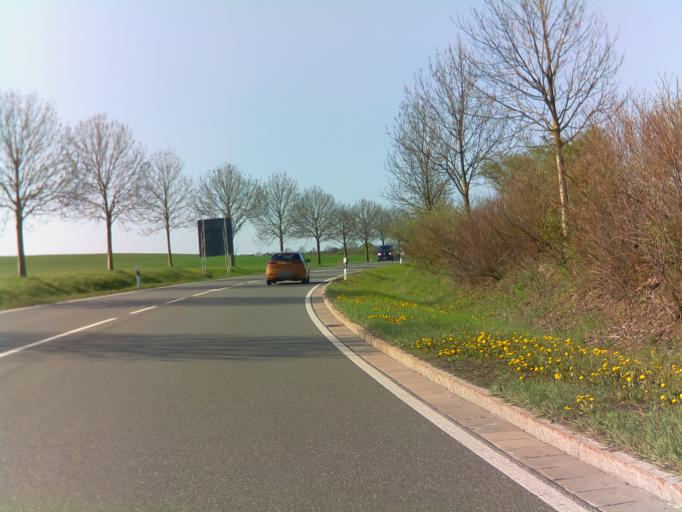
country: DE
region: Thuringia
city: Pormitz
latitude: 50.6094
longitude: 11.8251
